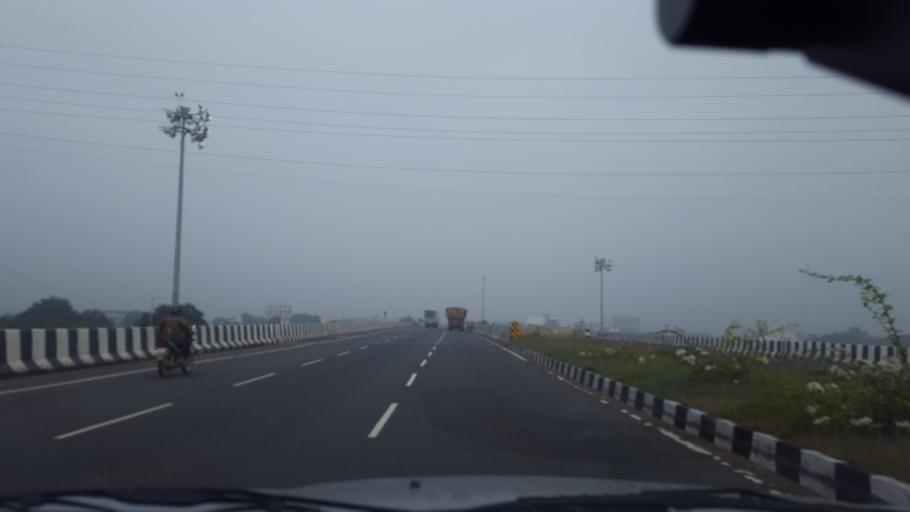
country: IN
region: Andhra Pradesh
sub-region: Prakasam
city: Ongole
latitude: 15.5322
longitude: 80.0526
